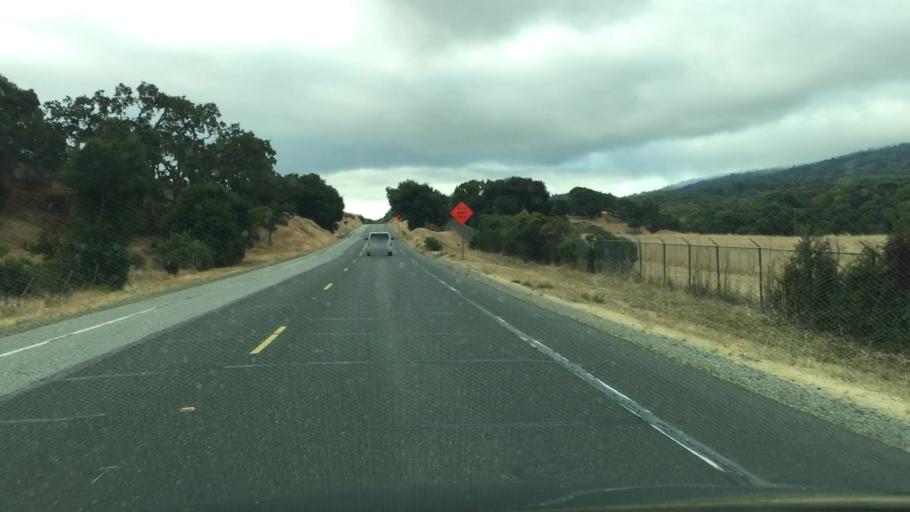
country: US
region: California
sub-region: San Mateo County
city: Emerald Lake Hills
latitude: 37.4754
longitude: -122.3082
